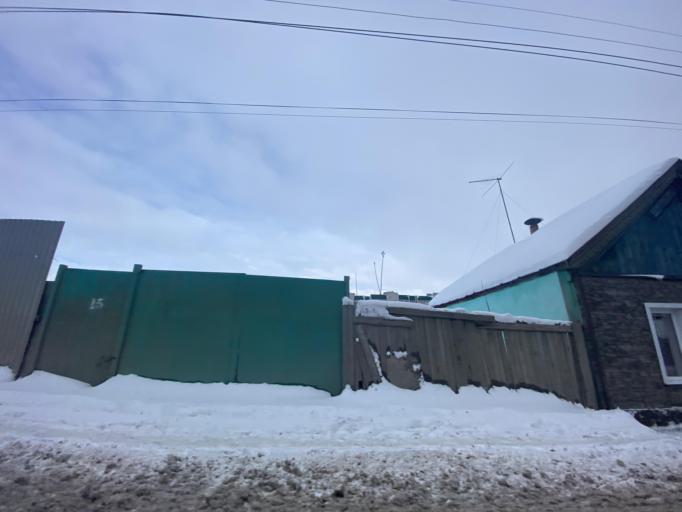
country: RU
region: Saratov
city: Engel's
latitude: 51.5017
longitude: 46.1075
